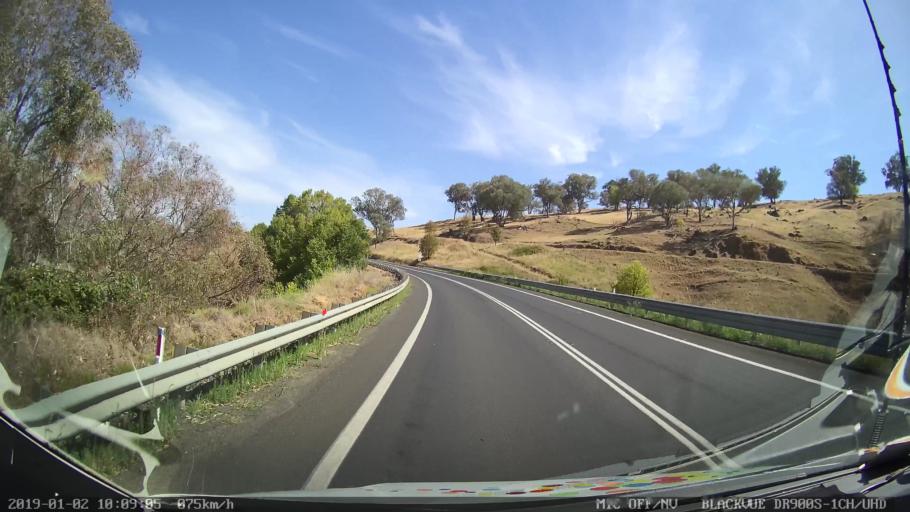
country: AU
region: New South Wales
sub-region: Gundagai
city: Gundagai
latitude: -35.1200
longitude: 148.1007
